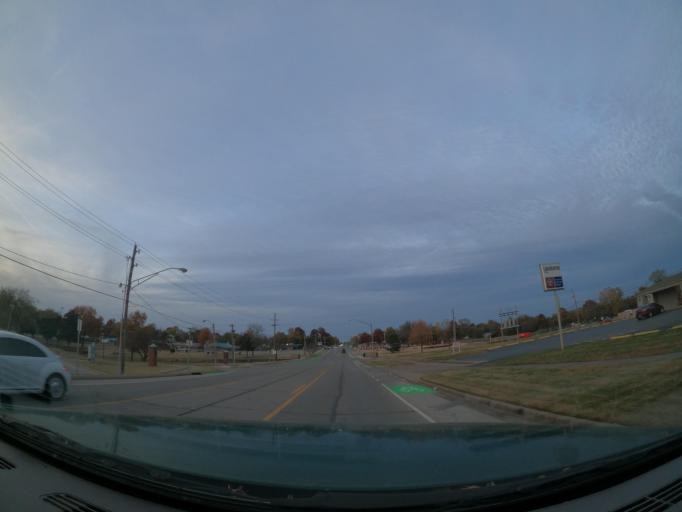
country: US
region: Oklahoma
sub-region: Tulsa County
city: Broken Arrow
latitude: 36.0402
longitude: -95.7908
